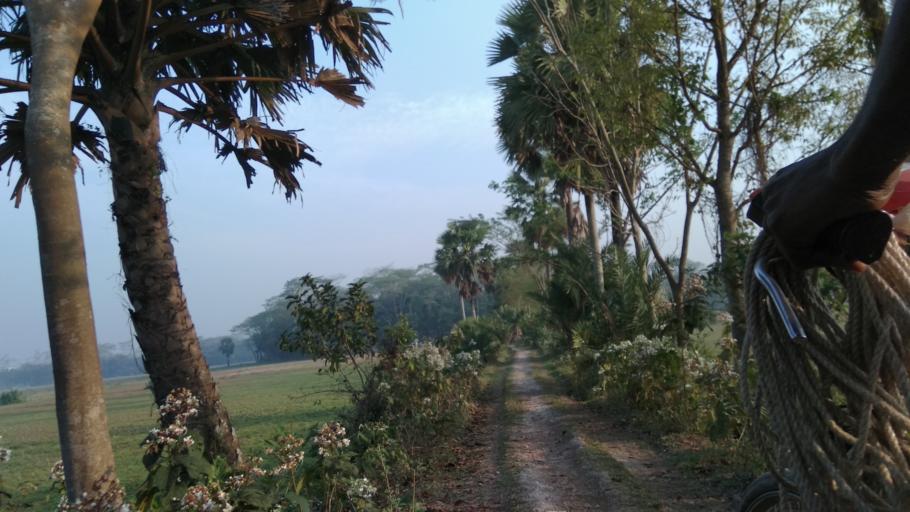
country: BD
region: Barisal
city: Mehendiganj
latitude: 22.9350
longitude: 90.4137
